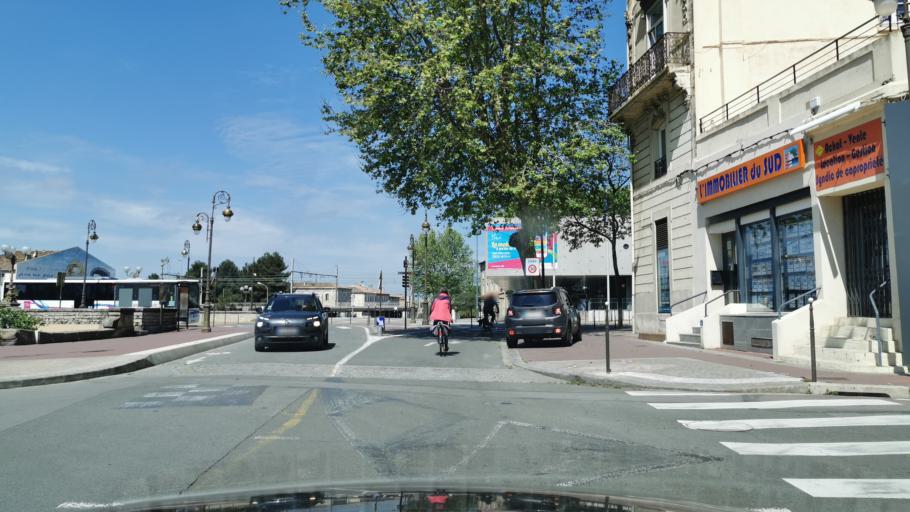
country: FR
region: Languedoc-Roussillon
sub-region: Departement de l'Aude
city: Narbonne
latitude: 43.1848
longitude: 3.0011
